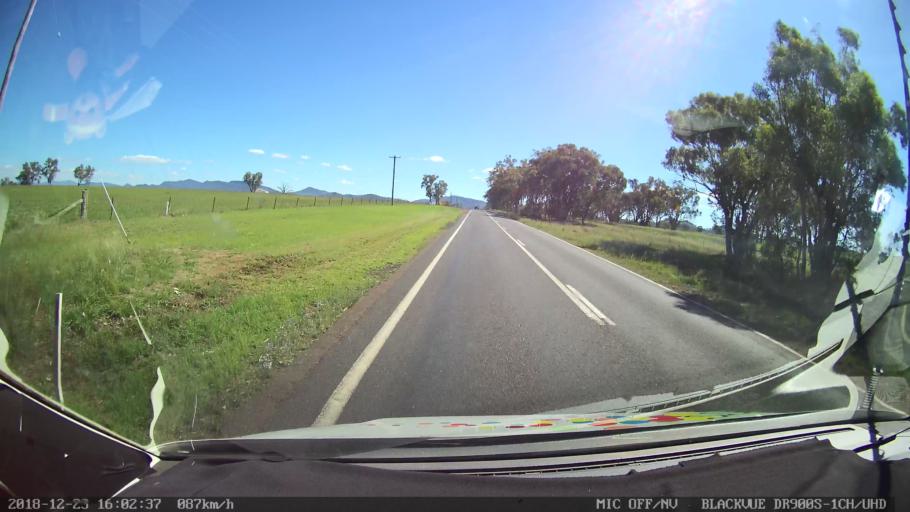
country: AU
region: New South Wales
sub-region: Tamworth Municipality
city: Phillip
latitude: -31.2342
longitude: 150.8076
